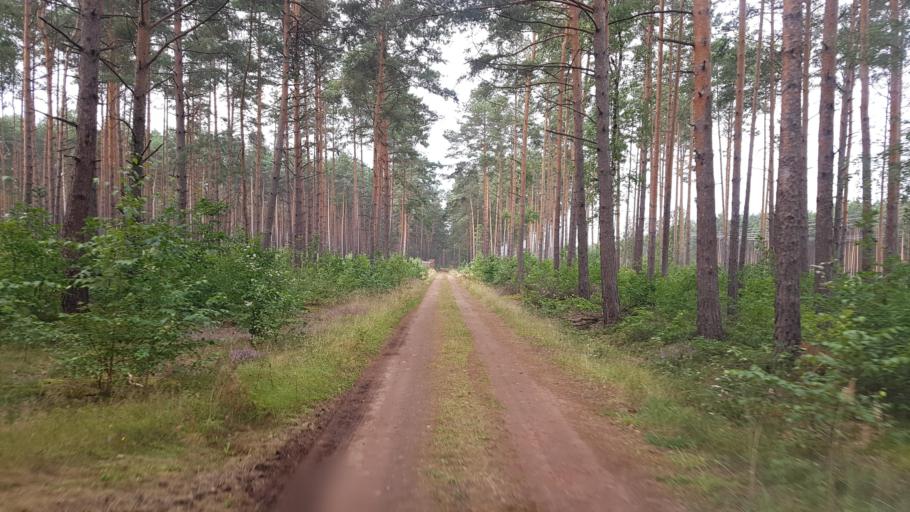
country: DE
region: Brandenburg
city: Hohenbucko
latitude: 51.7854
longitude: 13.5713
